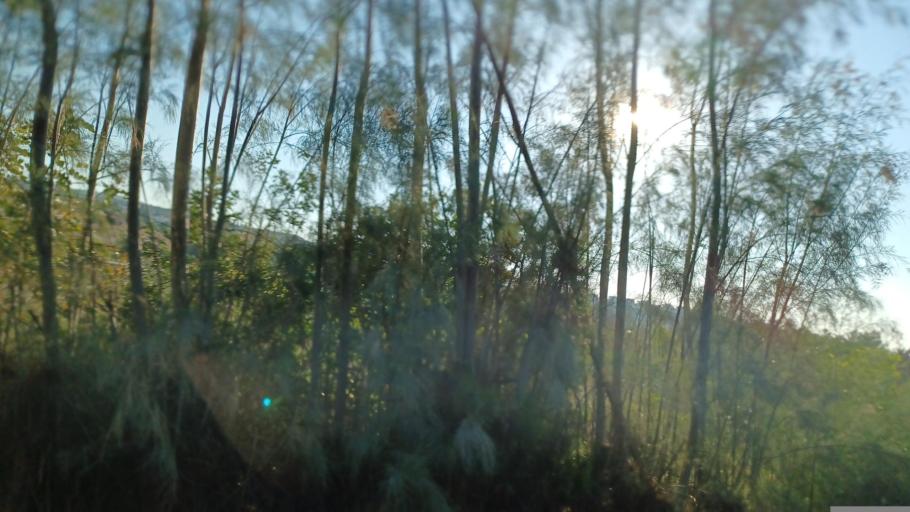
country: CY
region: Pafos
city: Pegeia
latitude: 34.8796
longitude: 32.3426
